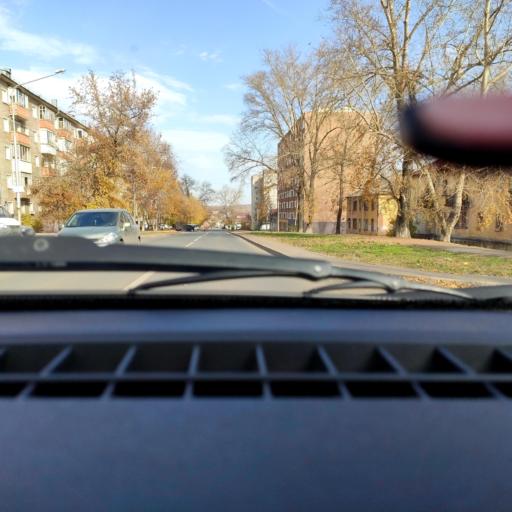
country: RU
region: Bashkortostan
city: Ufa
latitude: 54.8175
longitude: 56.1133
